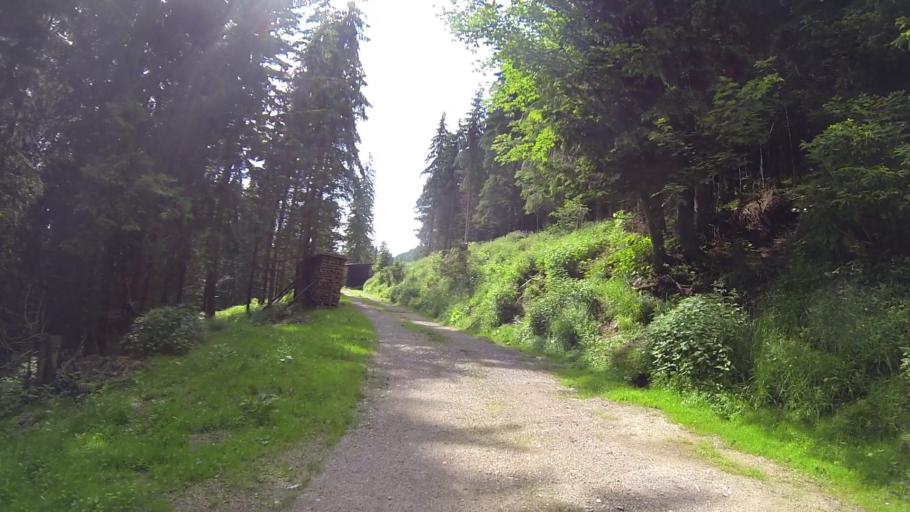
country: AT
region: Tyrol
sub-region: Politischer Bezirk Reutte
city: Breitenwang
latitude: 47.5029
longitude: 10.7762
